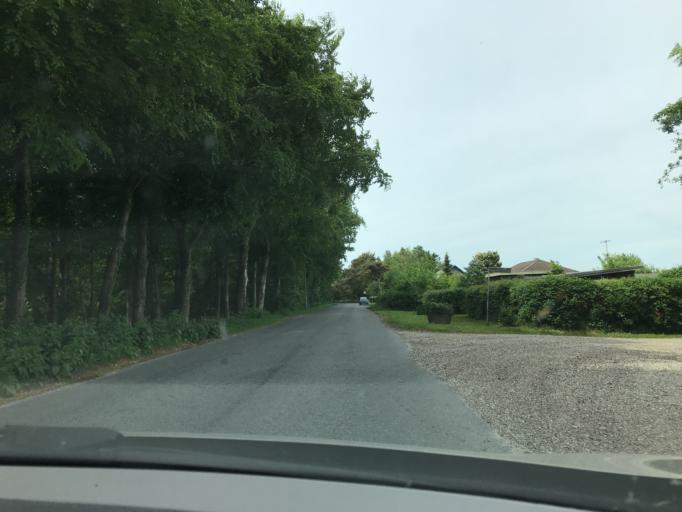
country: DK
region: Central Jutland
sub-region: Norddjurs Kommune
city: Allingabro
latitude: 56.6016
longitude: 10.3091
